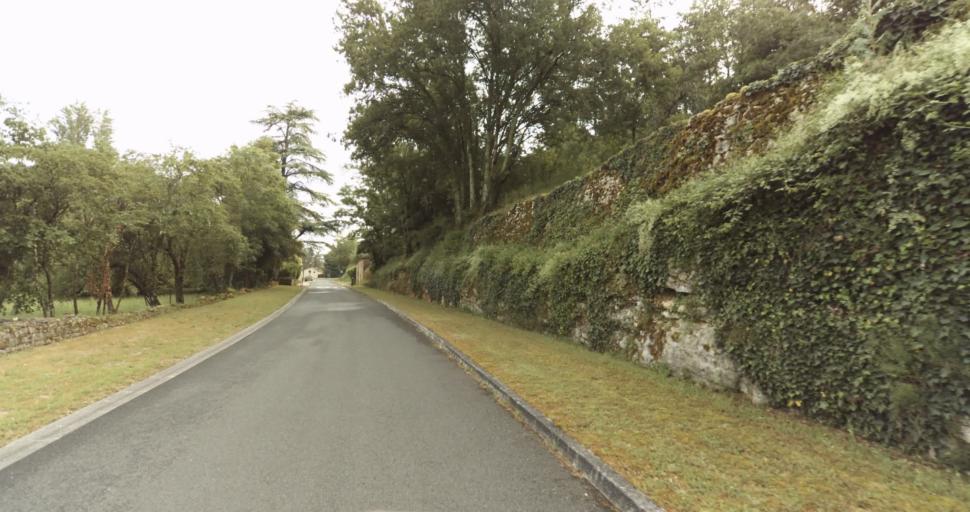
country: FR
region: Aquitaine
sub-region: Departement de la Dordogne
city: Lalinde
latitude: 44.9137
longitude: 0.8076
